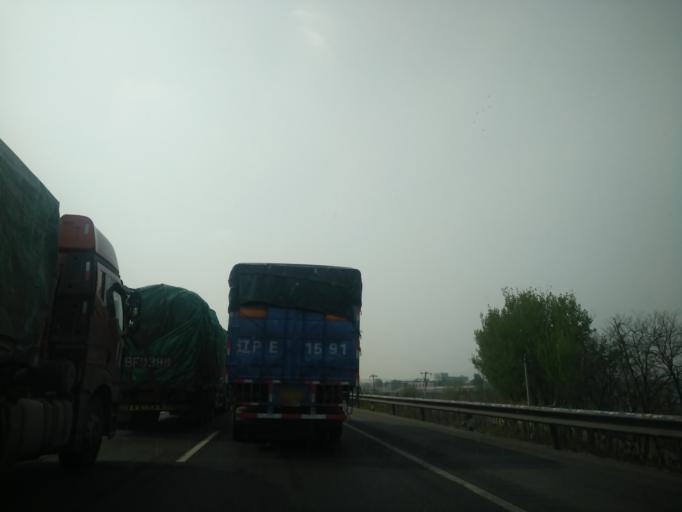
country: CN
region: Beijing
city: Zhangjiawan
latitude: 39.8333
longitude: 116.7103
